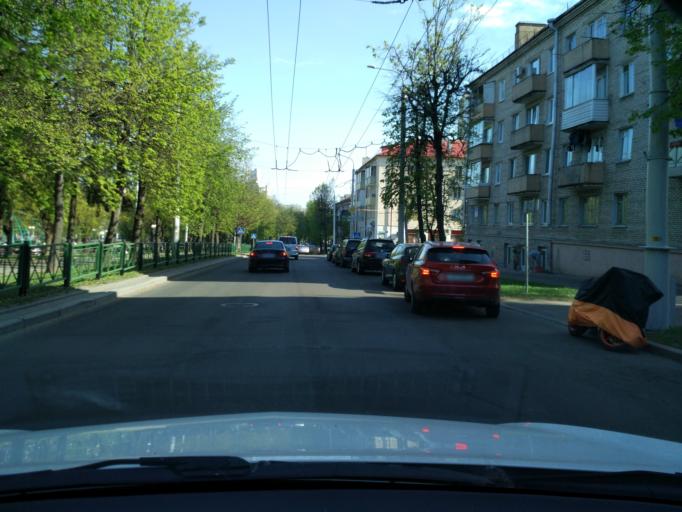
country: BY
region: Minsk
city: Minsk
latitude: 53.9297
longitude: 27.6095
